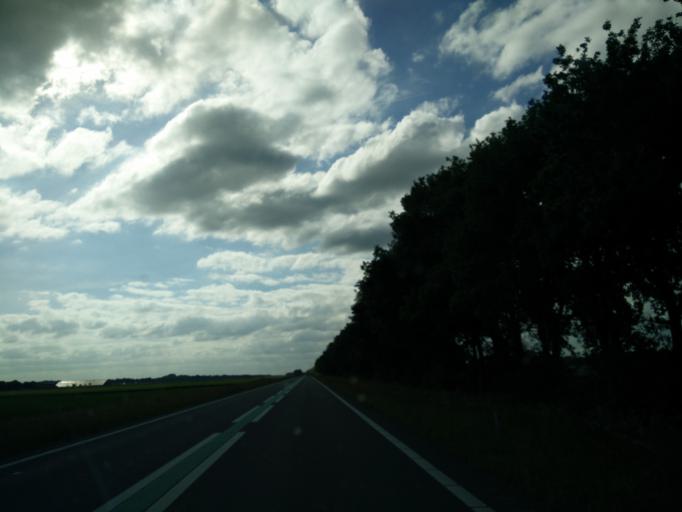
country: NL
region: Drenthe
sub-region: Gemeente Coevorden
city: Dalen
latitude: 52.8213
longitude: 6.6449
